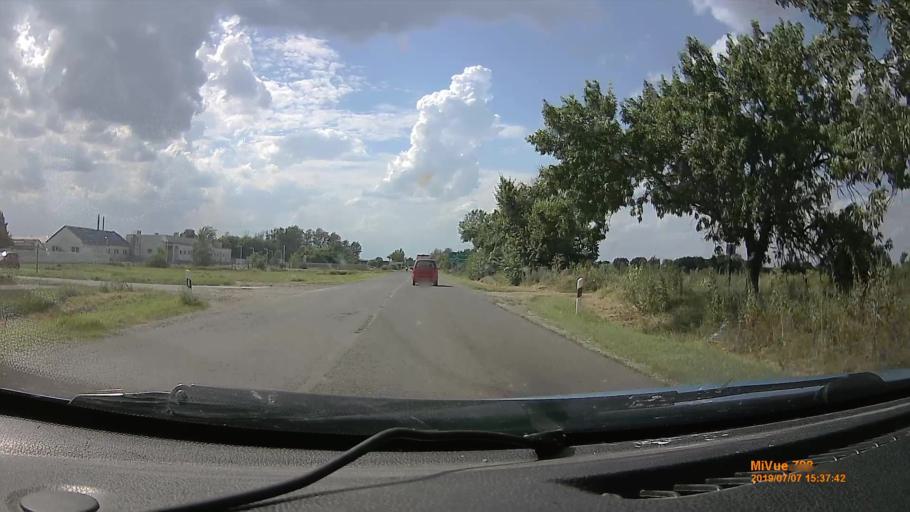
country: HU
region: Jasz-Nagykun-Szolnok
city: Jaszbereny
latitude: 47.4871
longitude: 19.9467
